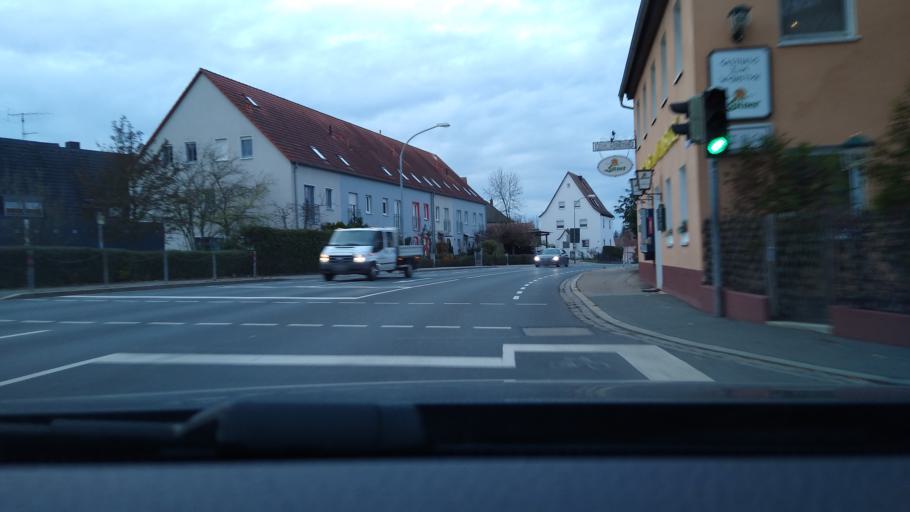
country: DE
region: Bavaria
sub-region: Regierungsbezirk Mittelfranken
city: Schwabach
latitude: 49.3285
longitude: 11.0121
